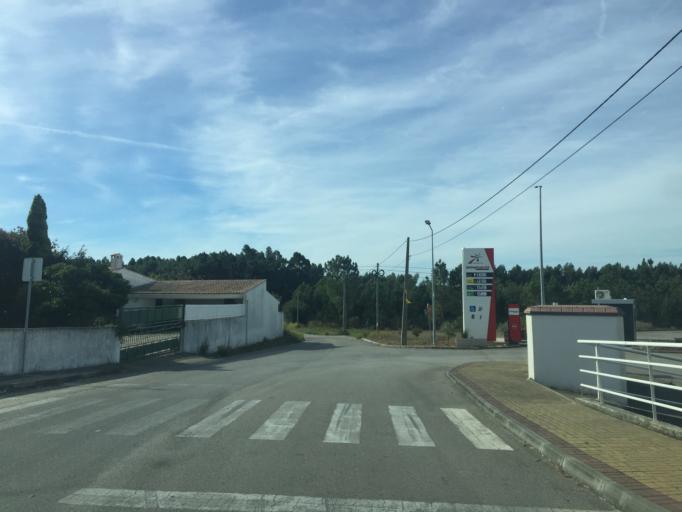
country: PT
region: Coimbra
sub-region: Figueira da Foz
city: Lavos
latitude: 40.0850
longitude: -8.8246
